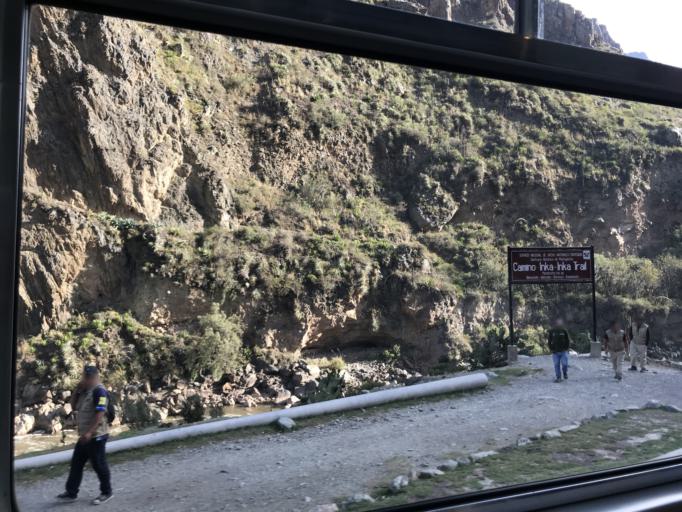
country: PE
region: Cusco
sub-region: Provincia de Urubamba
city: Ollantaytambo
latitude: -13.2153
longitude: -72.3829
